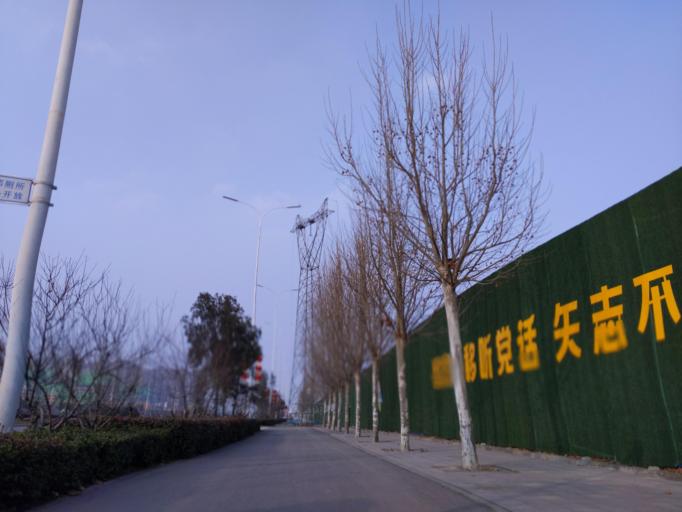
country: CN
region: Henan Sheng
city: Puyang
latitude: 35.8070
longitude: 115.0222
